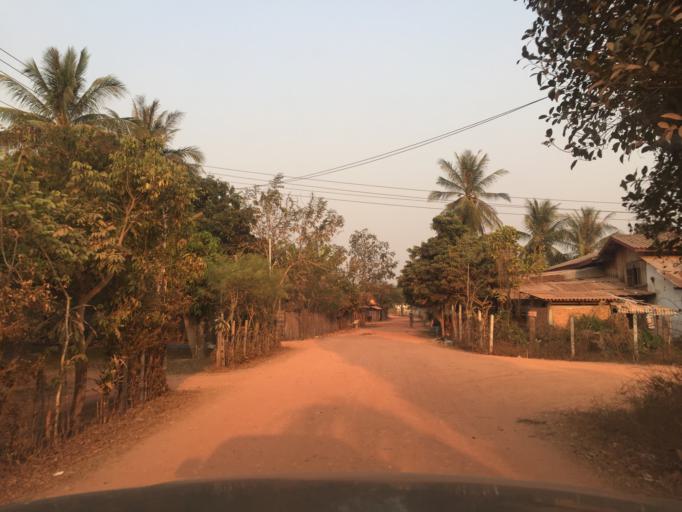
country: LA
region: Vientiane
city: Vientiane
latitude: 18.0621
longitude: 102.5210
